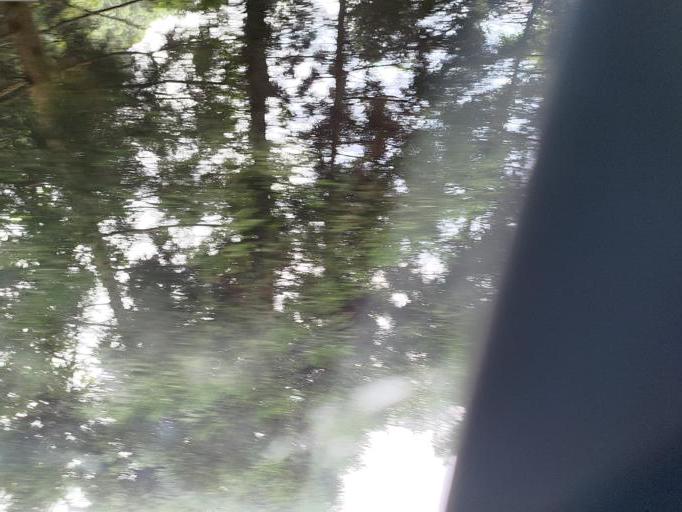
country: TW
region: Taiwan
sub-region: Hsinchu
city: Hsinchu
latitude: 24.6266
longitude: 121.0652
